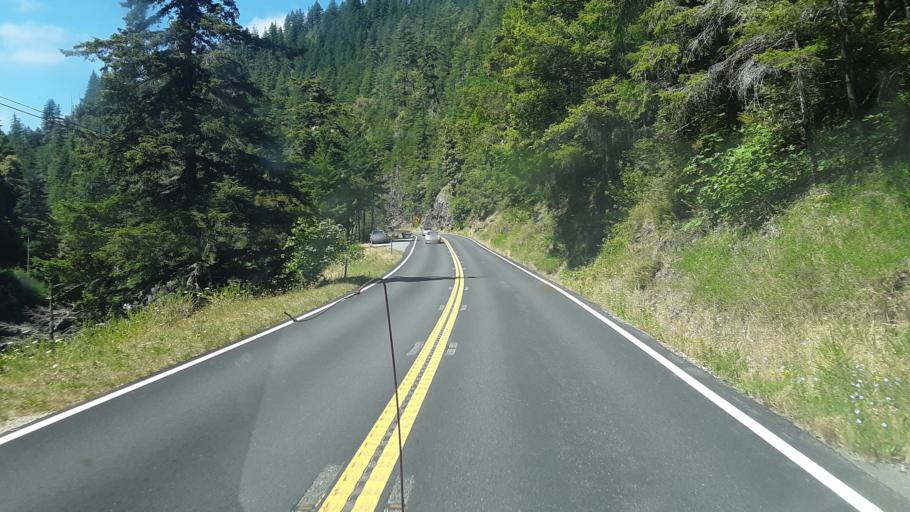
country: US
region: California
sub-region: Del Norte County
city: Bertsch-Oceanview
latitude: 41.8156
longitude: -124.0417
